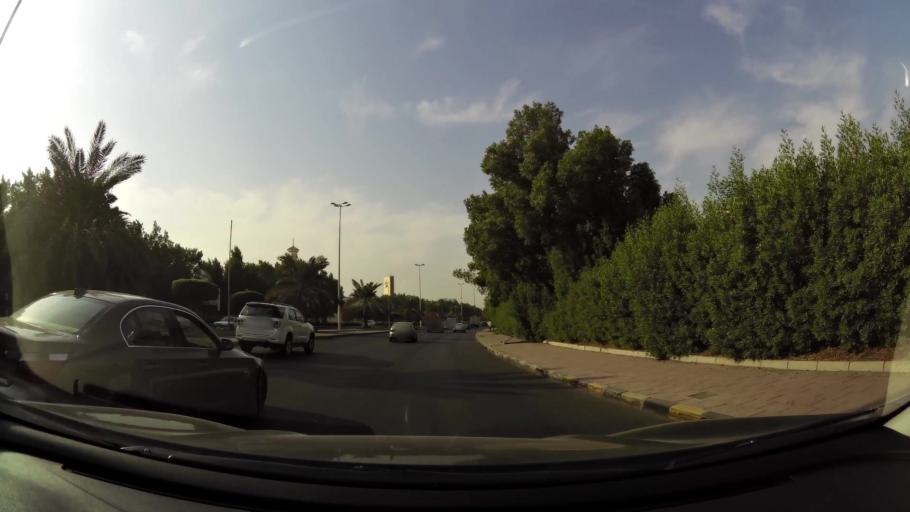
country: KW
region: Muhafazat Hawalli
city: Salwa
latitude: 29.2722
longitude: 48.0883
